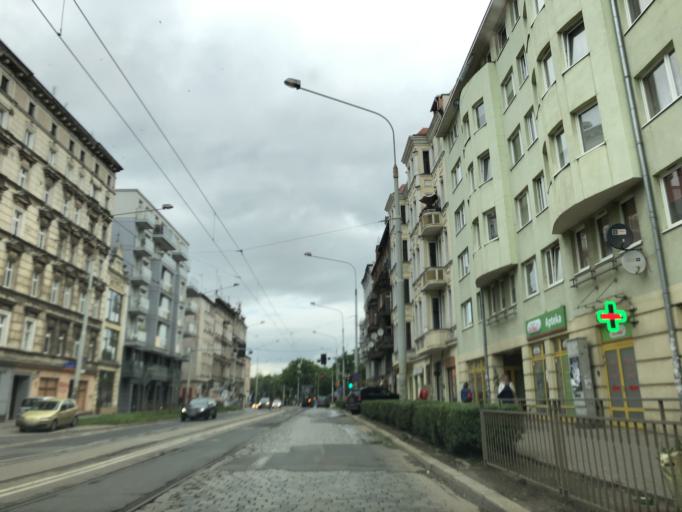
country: PL
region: Lower Silesian Voivodeship
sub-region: Powiat wroclawski
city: Wroclaw
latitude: 51.1208
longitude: 17.0311
